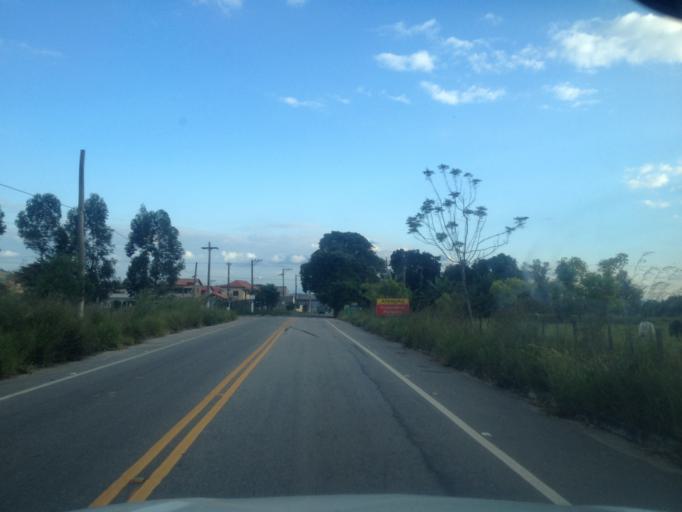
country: BR
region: Rio de Janeiro
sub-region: Quatis
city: Quatis
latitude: -22.4033
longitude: -44.2679
